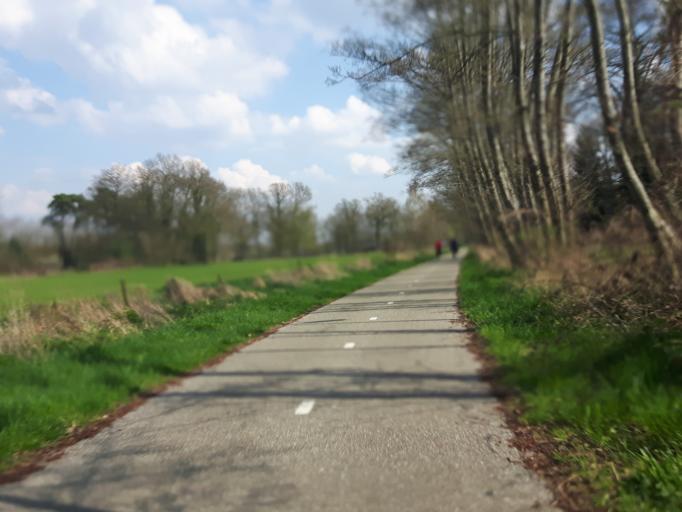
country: NL
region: Overijssel
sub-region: Gemeente Hengelo
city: Hengelo
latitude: 52.2051
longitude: 6.8209
